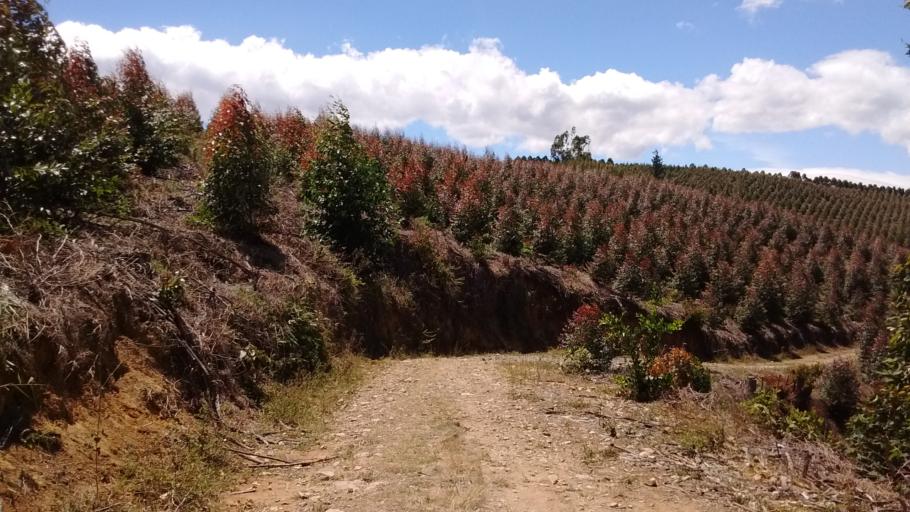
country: CO
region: Cauca
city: Popayan
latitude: 2.4607
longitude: -76.5668
